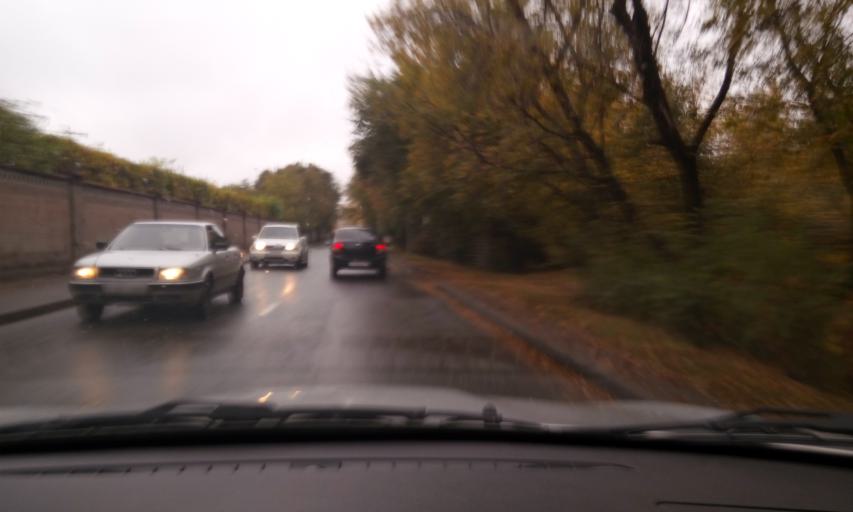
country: KZ
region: Astana Qalasy
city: Astana
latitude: 51.1427
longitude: 71.4316
